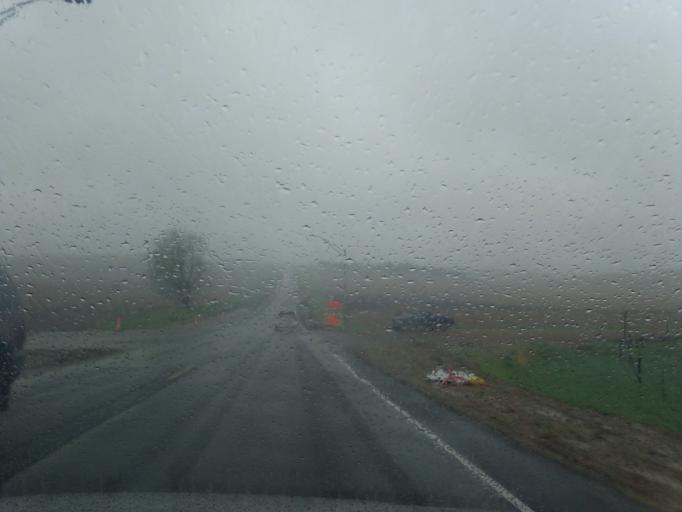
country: US
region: Nebraska
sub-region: Wayne County
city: Wayne
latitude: 42.1779
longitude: -97.1845
